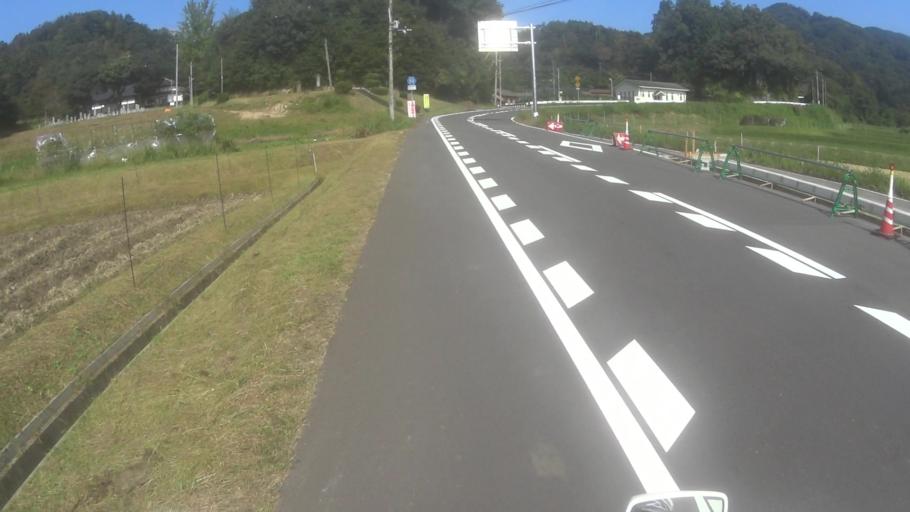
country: JP
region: Kyoto
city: Miyazu
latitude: 35.6166
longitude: 135.1301
